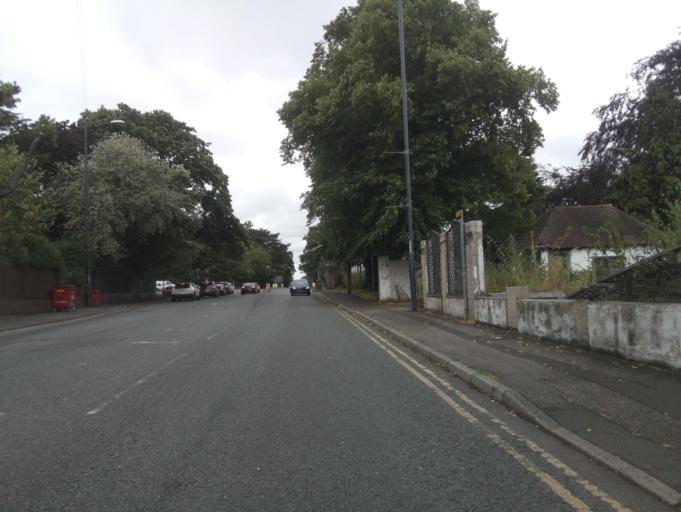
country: GB
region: England
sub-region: Derby
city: Derby
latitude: 52.9074
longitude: -1.5022
